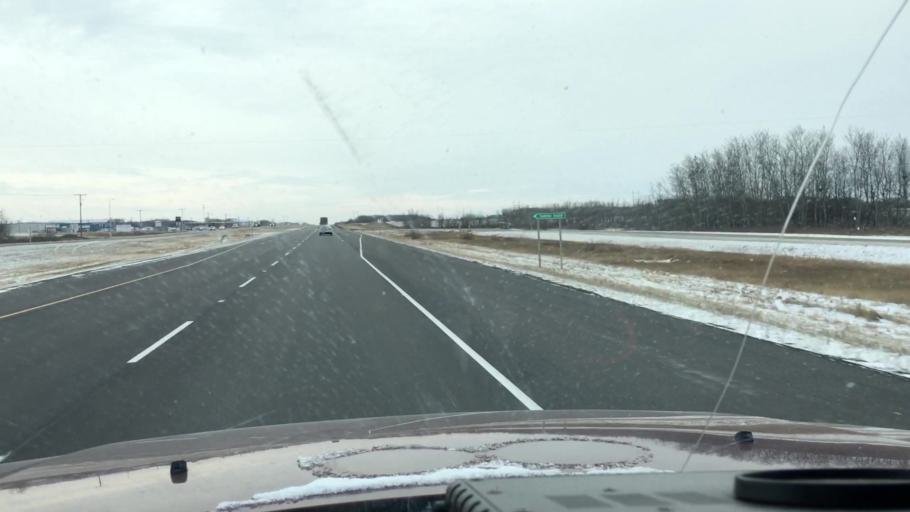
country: CA
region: Saskatchewan
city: Saskatoon
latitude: 51.9711
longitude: -106.5546
